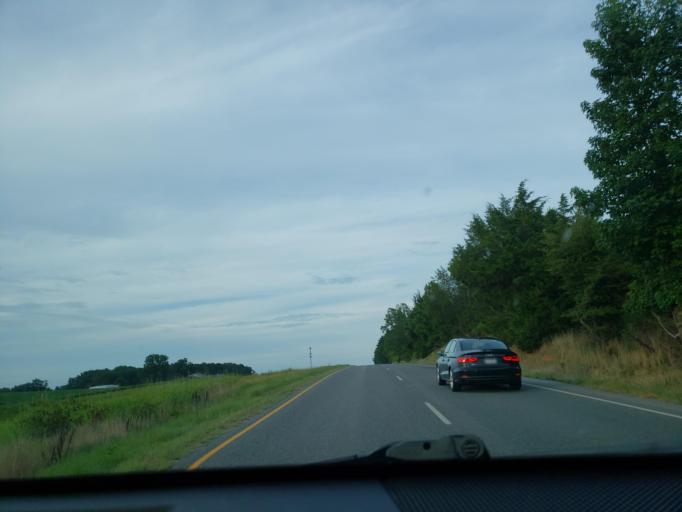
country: US
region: Virginia
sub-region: Brunswick County
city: Lawrenceville
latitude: 36.7326
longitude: -77.9075
